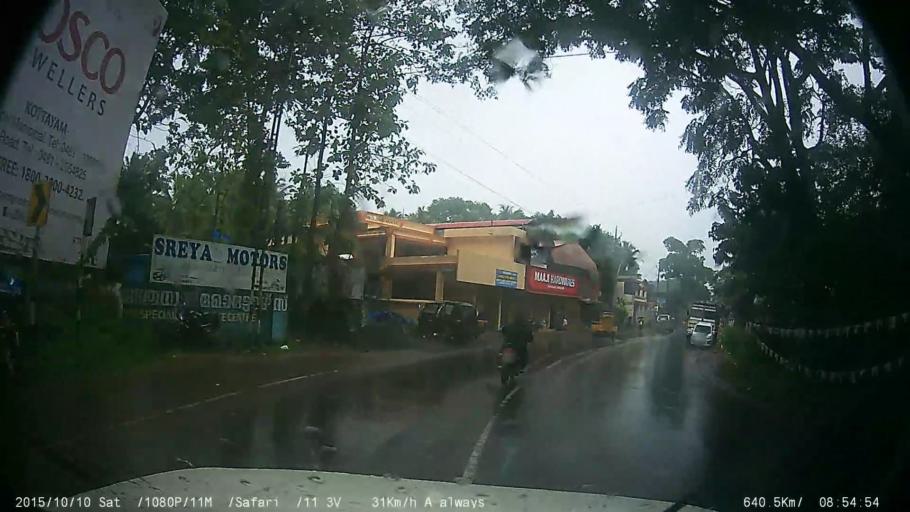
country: IN
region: Kerala
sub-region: Kottayam
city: Palackattumala
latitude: 9.7023
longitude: 76.5480
